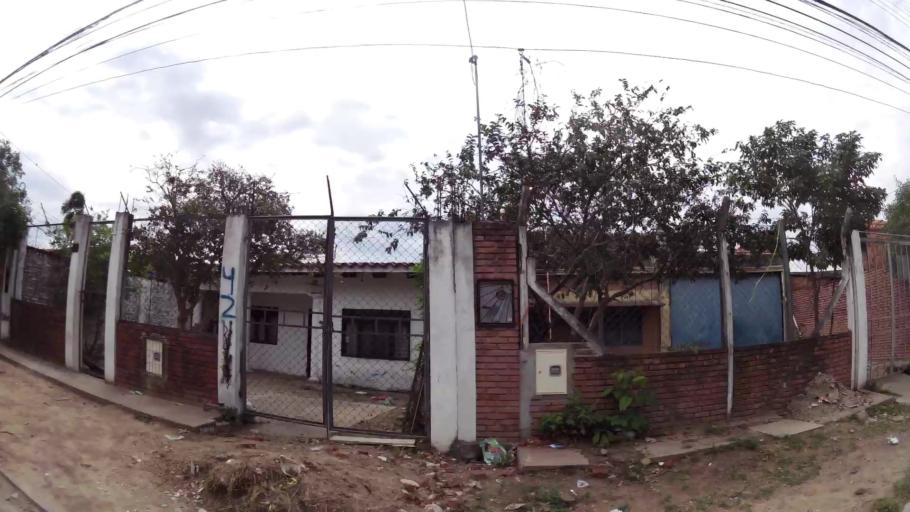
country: BO
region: Santa Cruz
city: Santa Cruz de la Sierra
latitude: -17.7464
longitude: -63.1916
